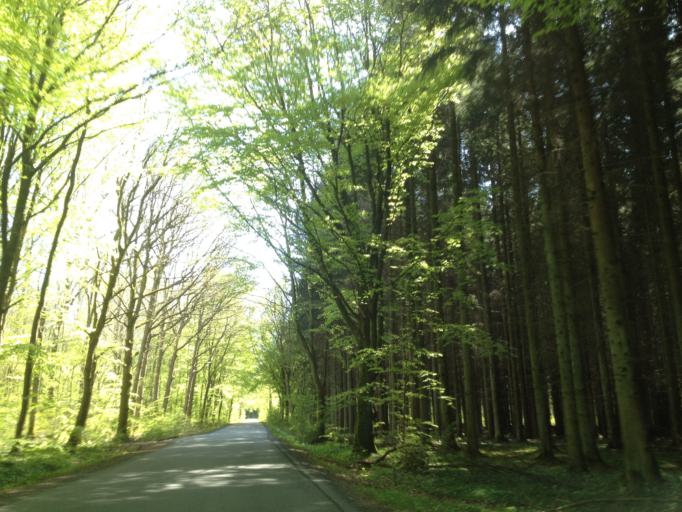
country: DK
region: Zealand
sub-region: Roskilde Kommune
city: Viby
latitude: 55.5248
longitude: 12.0156
